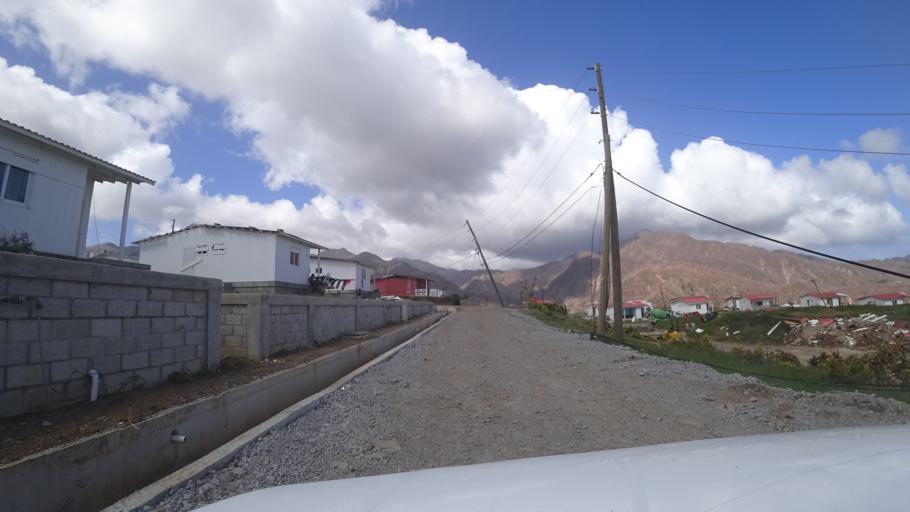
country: DM
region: Saint Patrick
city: Berekua
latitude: 15.2454
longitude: -61.3231
